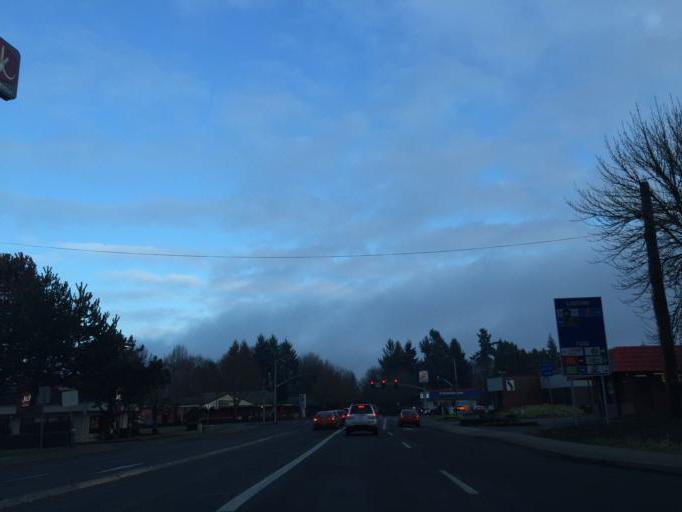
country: US
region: Washington
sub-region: Thurston County
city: Tumwater
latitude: 46.9999
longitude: -122.9103
